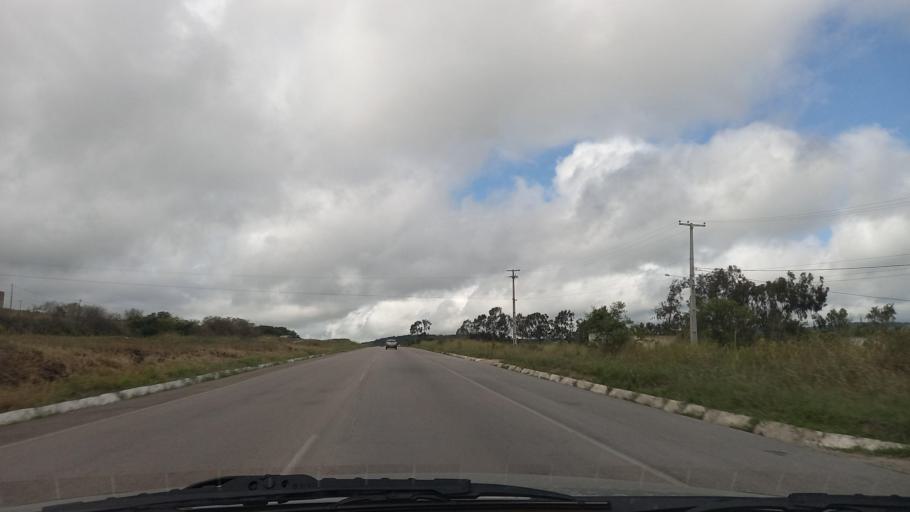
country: BR
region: Pernambuco
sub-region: Caruaru
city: Caruaru
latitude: -8.3176
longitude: -35.9914
